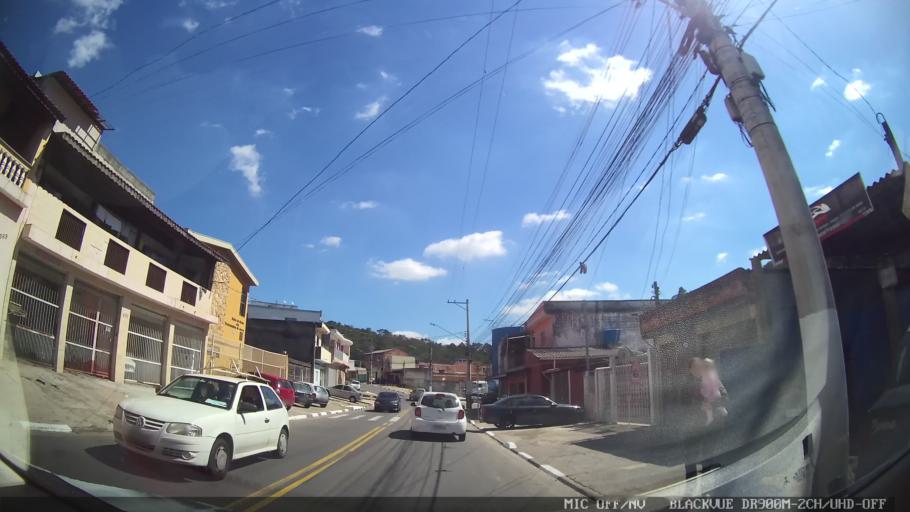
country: BR
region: Sao Paulo
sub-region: Cajamar
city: Cajamar
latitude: -23.4247
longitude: -46.8281
